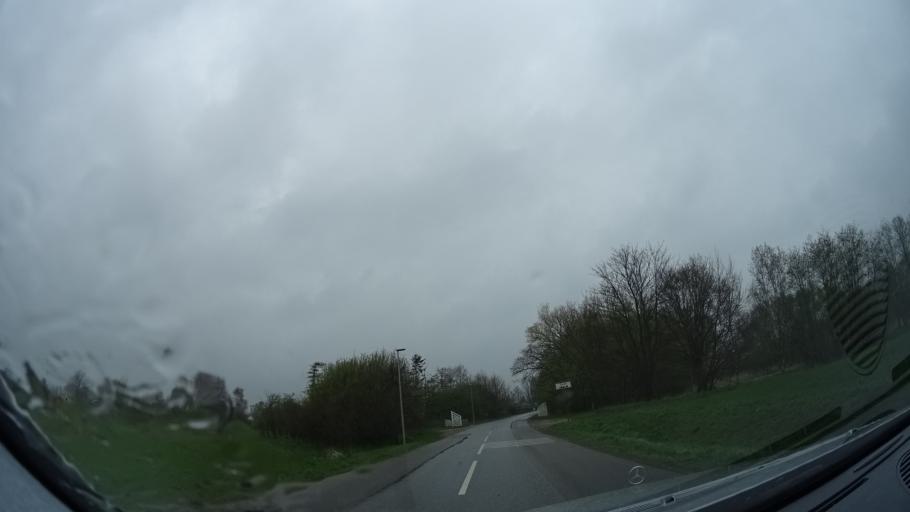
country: DK
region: Zealand
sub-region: Holbaek Kommune
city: Holbaek
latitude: 55.7065
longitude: 11.6257
